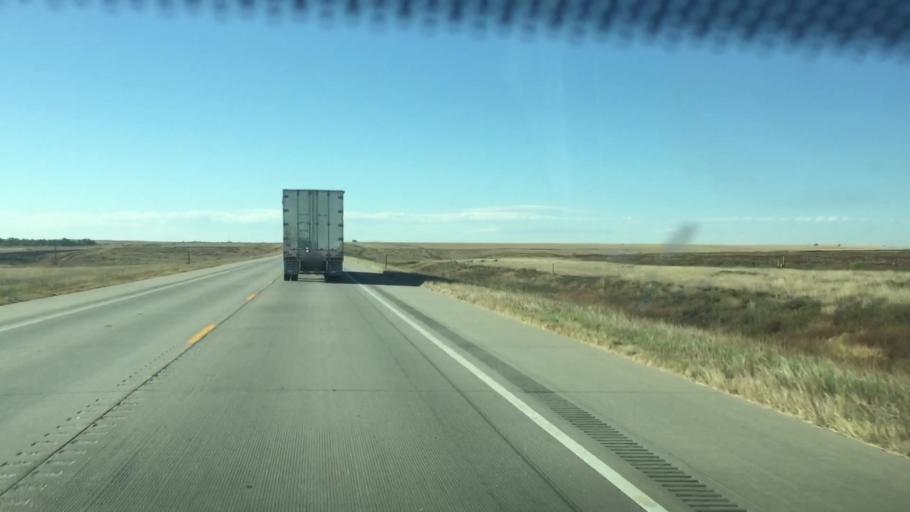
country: US
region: Colorado
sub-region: Kiowa County
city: Eads
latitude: 38.8007
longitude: -102.9574
